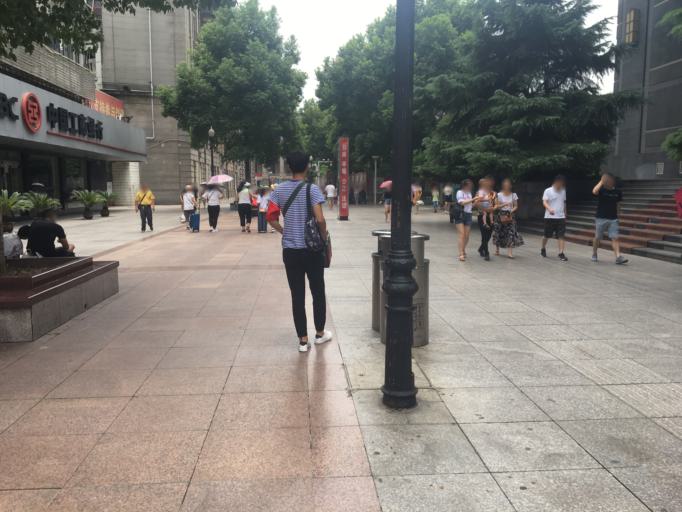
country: CN
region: Hubei
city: Wuhan
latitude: 30.5801
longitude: 114.2901
